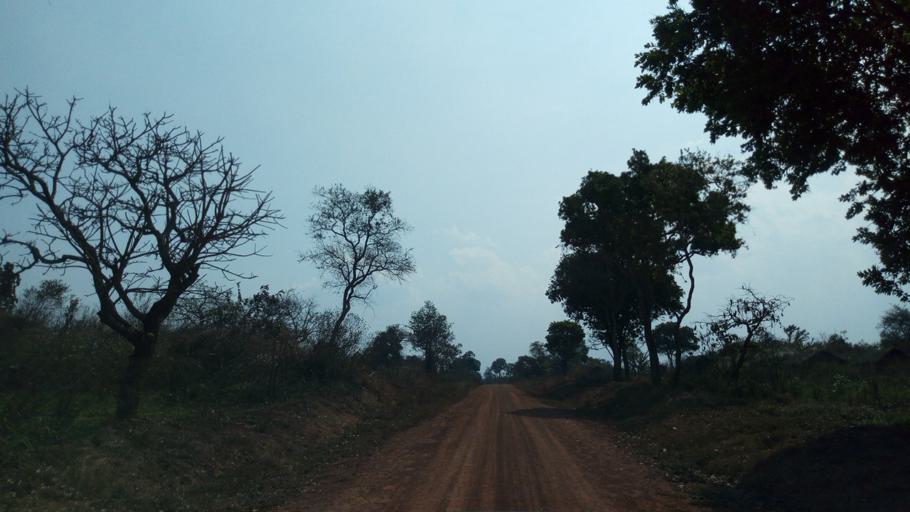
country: CD
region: Katanga
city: Kalemie
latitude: -5.5494
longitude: 28.9983
